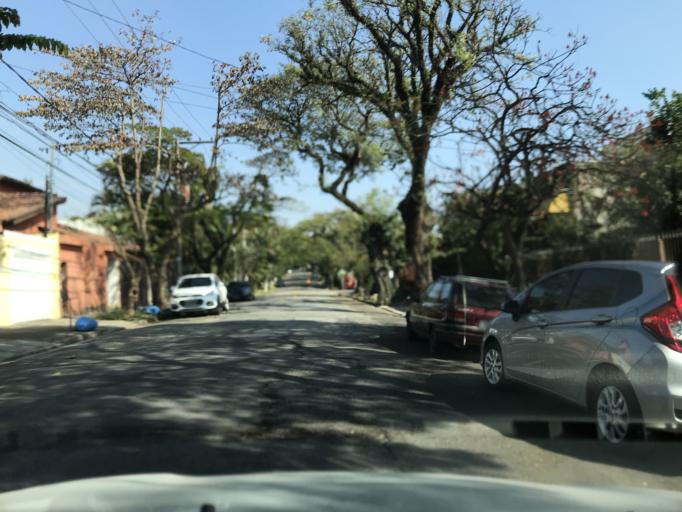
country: BR
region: Sao Paulo
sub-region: Osasco
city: Osasco
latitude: -23.5786
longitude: -46.7230
